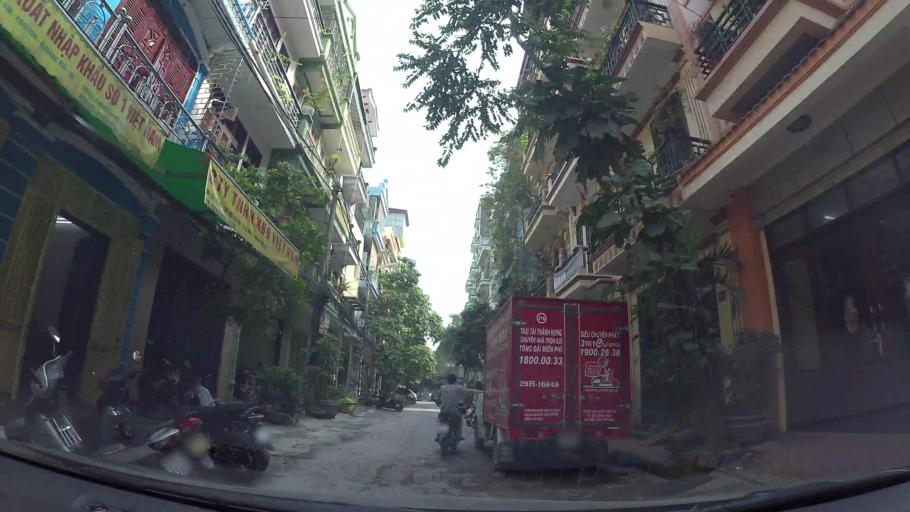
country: VN
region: Ha Noi
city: Van Dien
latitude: 20.9739
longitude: 105.8366
